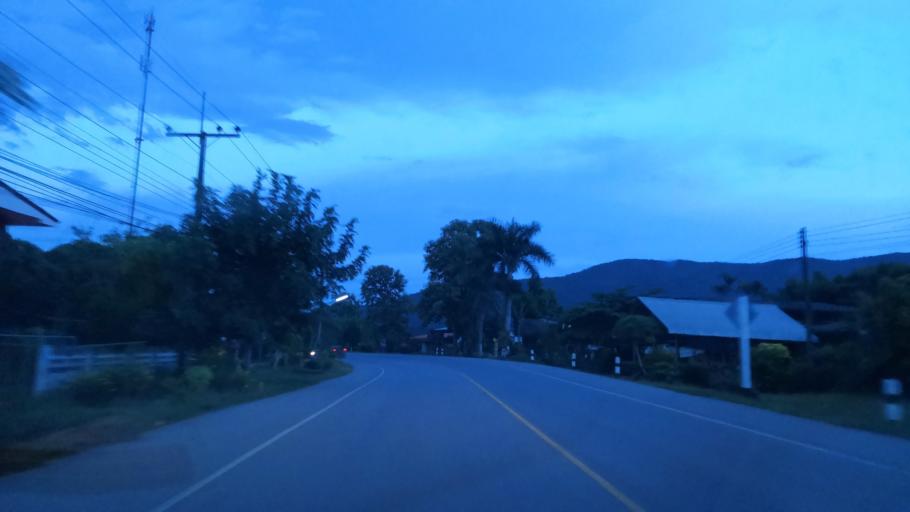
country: TH
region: Chiang Rai
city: Wiang Chiang Rung
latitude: 19.9653
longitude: 100.0087
